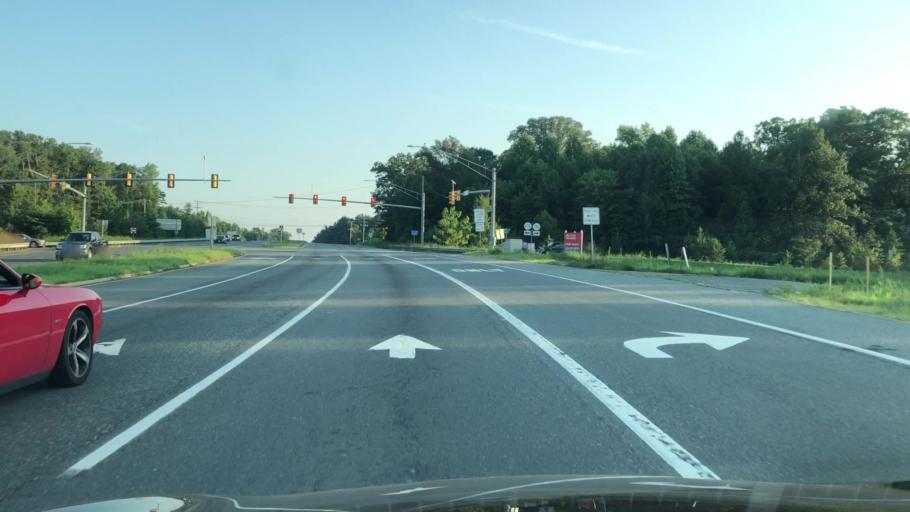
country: US
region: Virginia
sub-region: Stafford County
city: Falmouth
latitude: 38.3647
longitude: -77.4570
